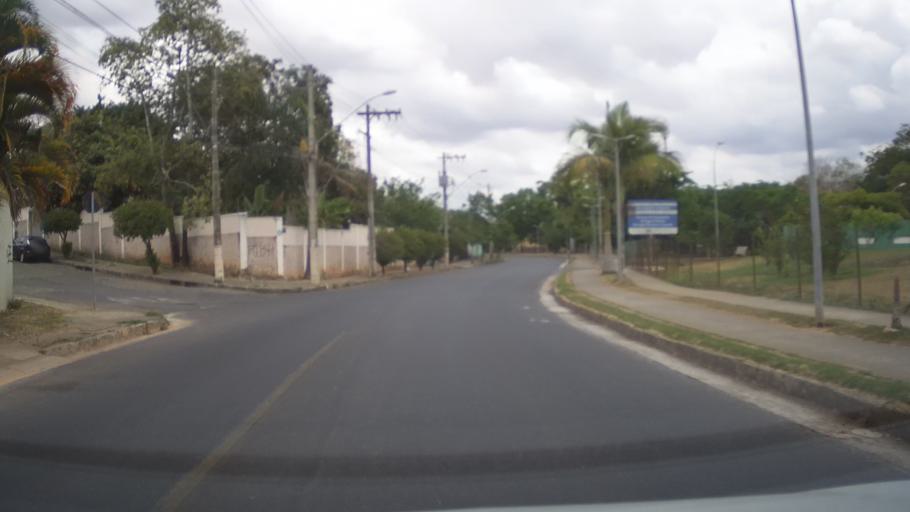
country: BR
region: Minas Gerais
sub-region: Belo Horizonte
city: Belo Horizonte
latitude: -19.8570
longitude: -43.9949
